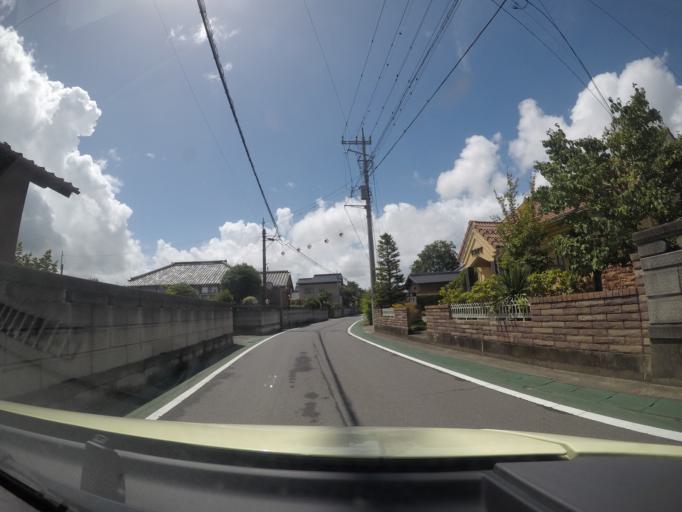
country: JP
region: Ibaraki
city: Mitsukaido
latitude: 36.0687
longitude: 140.0039
